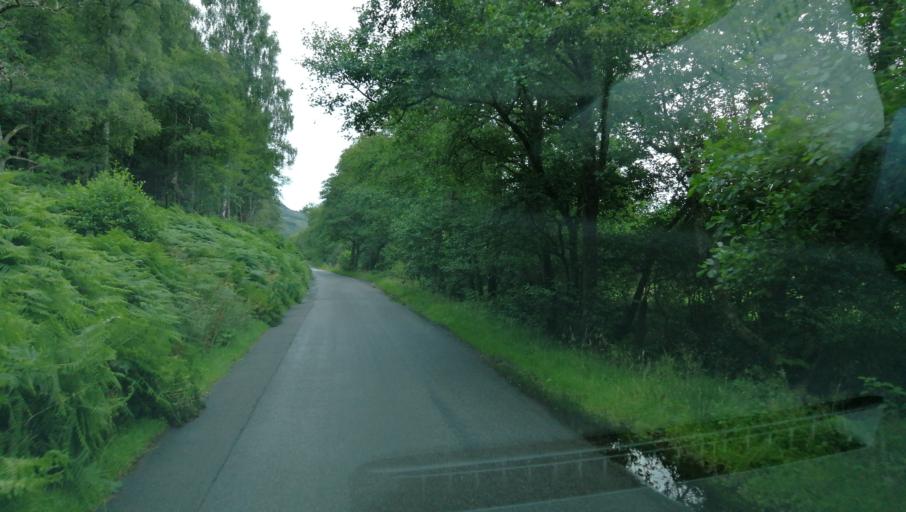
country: GB
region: Scotland
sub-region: Highland
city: Beauly
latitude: 57.3370
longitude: -4.7809
